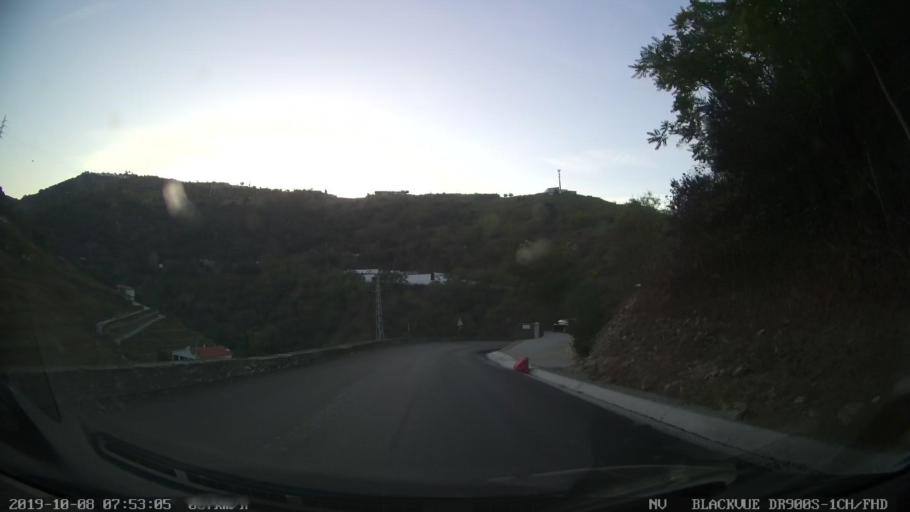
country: PT
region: Vila Real
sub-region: Sabrosa
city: Vilela
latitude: 41.1976
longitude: -7.5479
